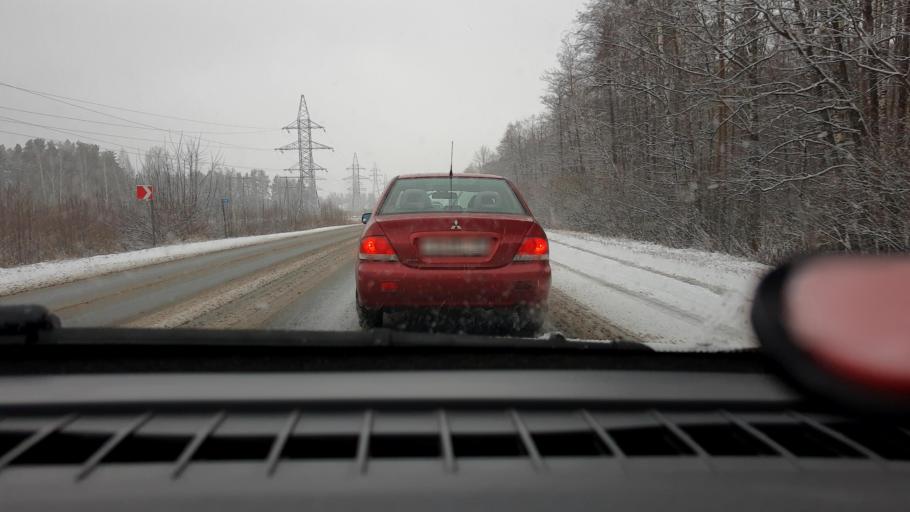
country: RU
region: Nizjnij Novgorod
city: Lukino
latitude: 56.4282
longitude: 43.6262
